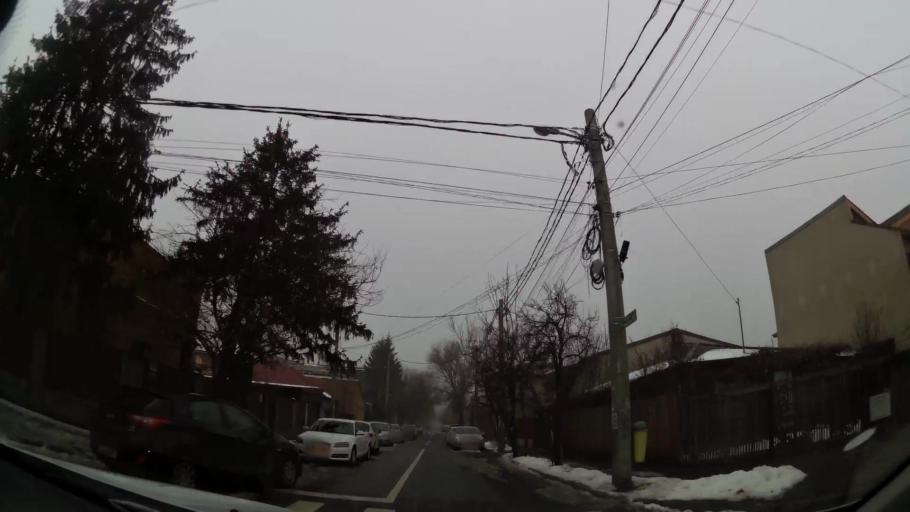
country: RO
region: Ilfov
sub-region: Comuna Chiajna
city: Rosu
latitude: 44.4761
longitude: 26.0398
